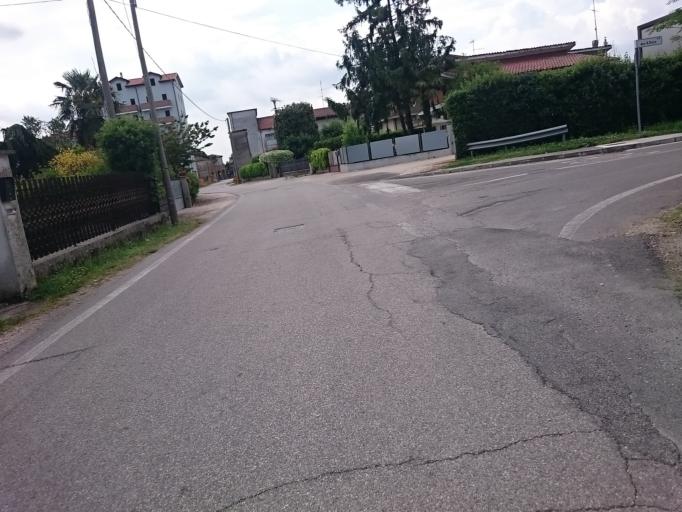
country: IT
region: Veneto
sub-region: Provincia di Padova
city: Ponso
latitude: 45.1902
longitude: 11.5884
